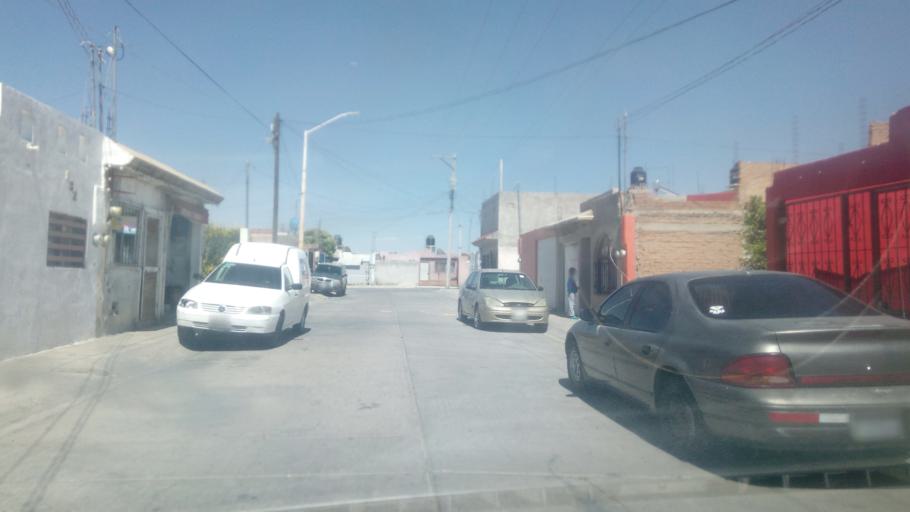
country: MX
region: Durango
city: Victoria de Durango
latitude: 24.0046
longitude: -104.6252
